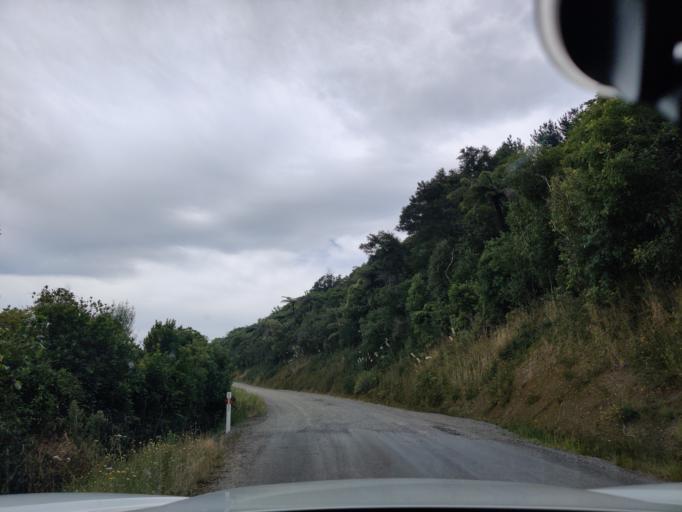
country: NZ
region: Wellington
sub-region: Masterton District
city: Masterton
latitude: -41.0377
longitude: 175.4163
